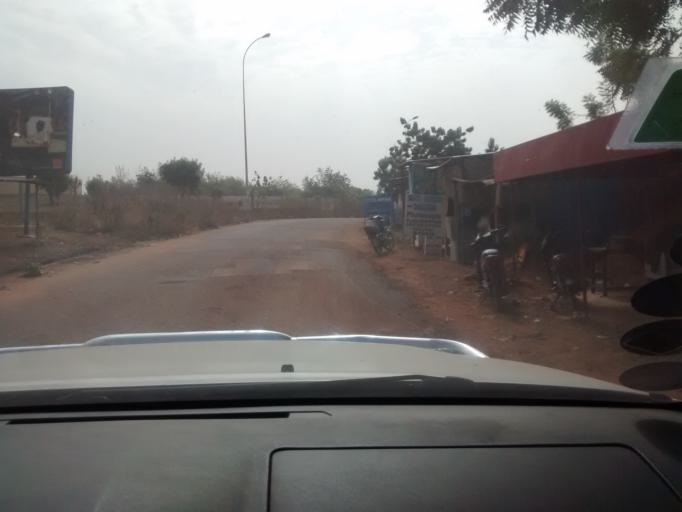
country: ML
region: Bamako
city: Bamako
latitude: 12.6153
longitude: -7.9854
